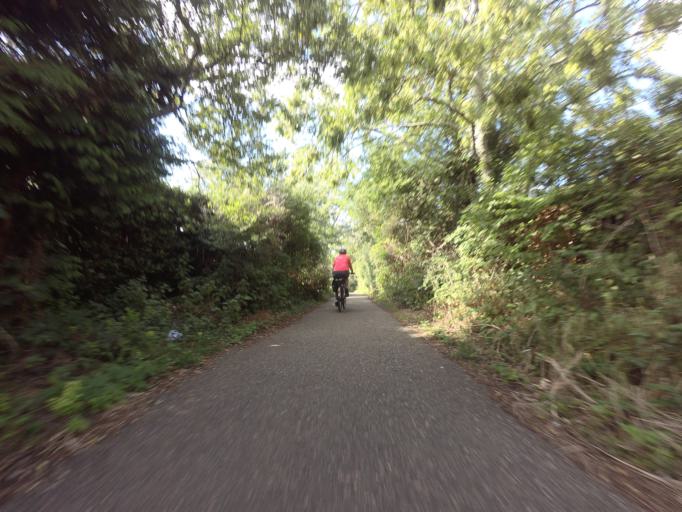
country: GB
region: England
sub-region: East Sussex
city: Hailsham
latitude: 50.8777
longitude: 0.2496
